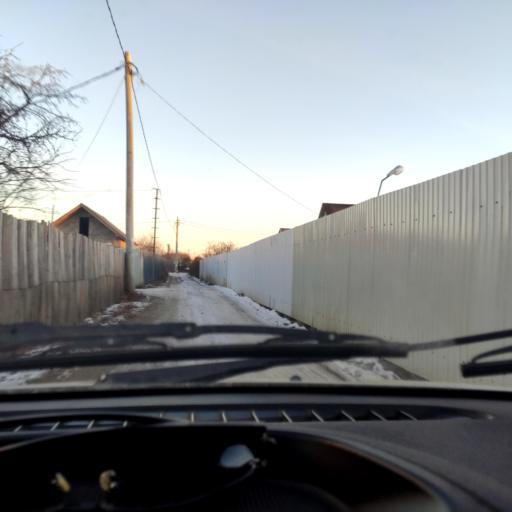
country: RU
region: Samara
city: Tol'yatti
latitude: 53.5421
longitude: 49.4317
